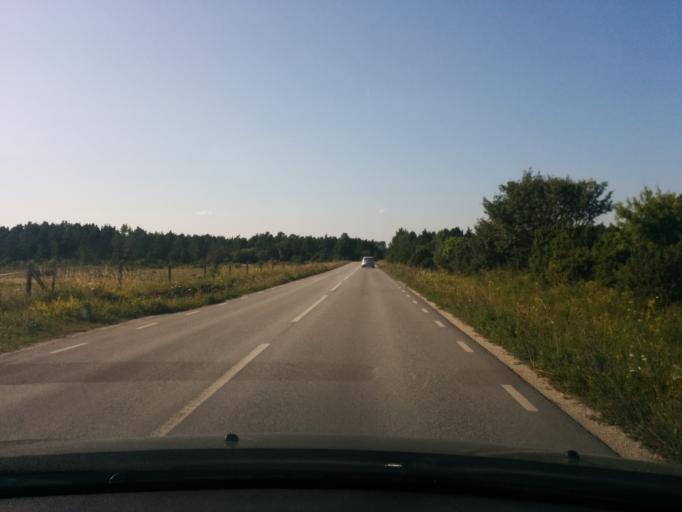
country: SE
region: Gotland
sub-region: Gotland
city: Slite
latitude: 57.6747
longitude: 18.7708
